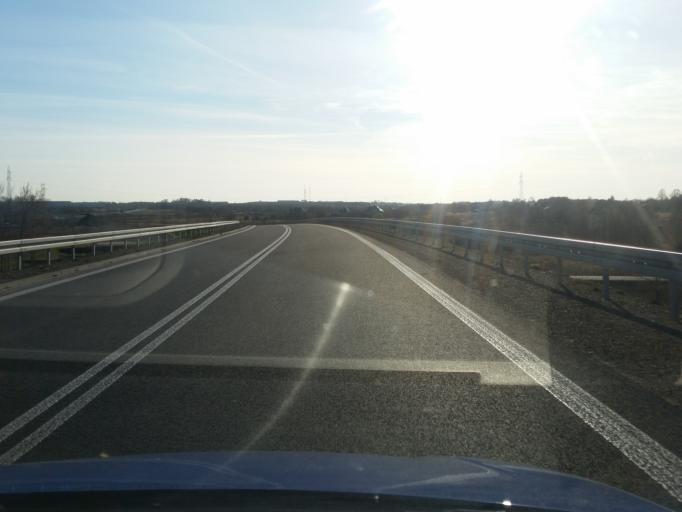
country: PL
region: Lodz Voivodeship
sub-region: Powiat radomszczanski
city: Radomsko
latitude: 51.1074
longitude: 19.4337
